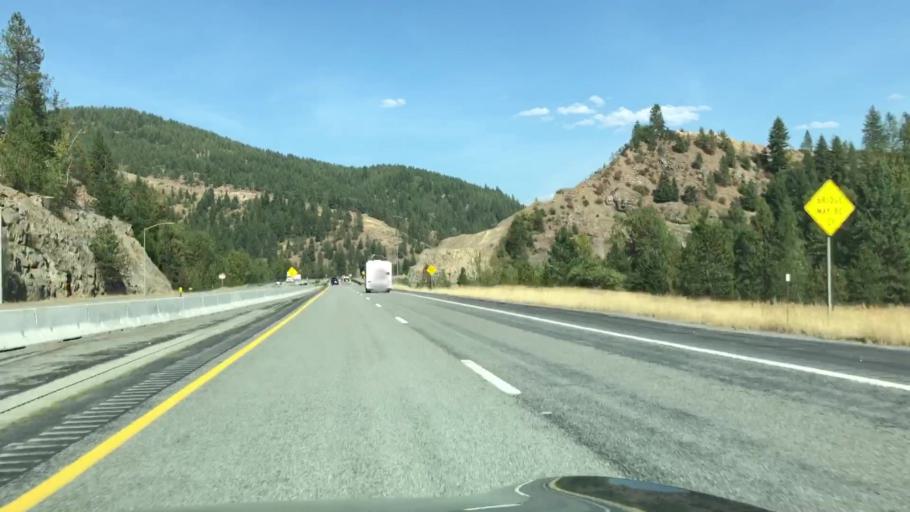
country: US
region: Idaho
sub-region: Shoshone County
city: Pinehurst
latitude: 47.5450
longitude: -116.2297
